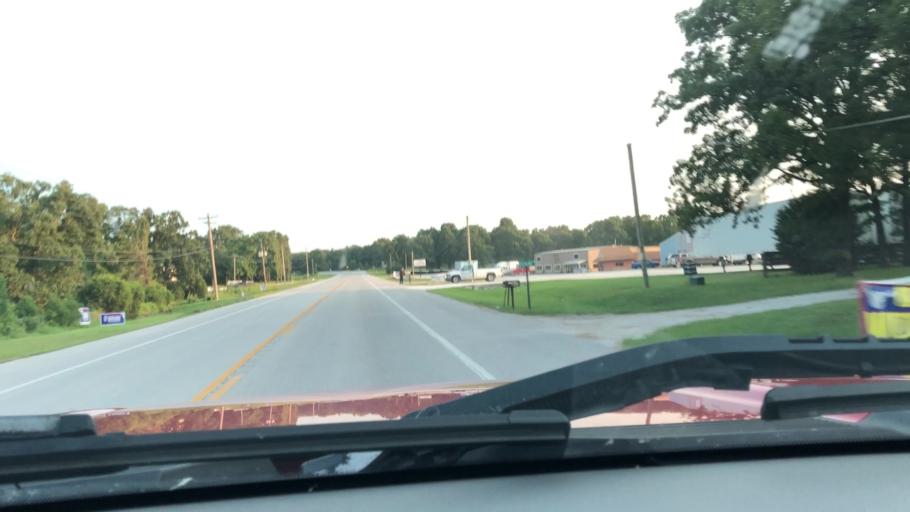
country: US
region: Missouri
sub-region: Jasper County
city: Duquesne
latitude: 36.9845
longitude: -94.4638
